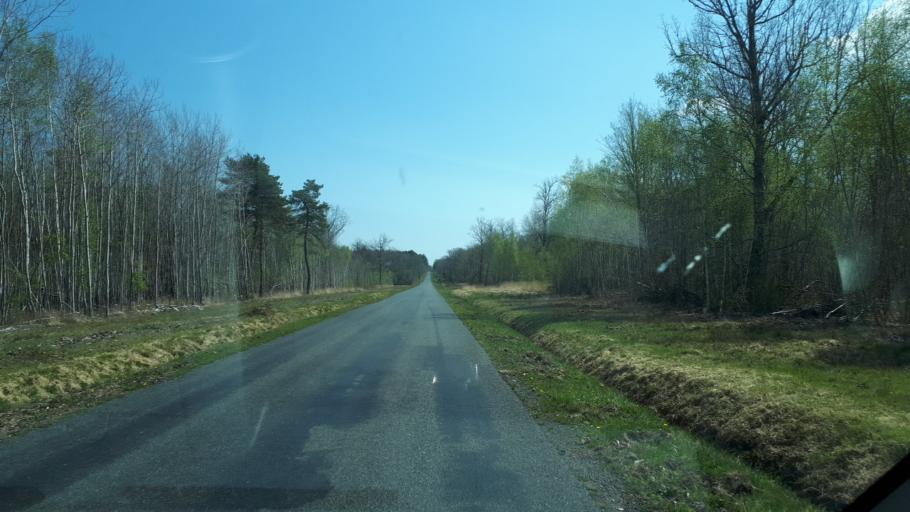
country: FR
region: Centre
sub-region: Departement du Cher
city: Neuvy-sur-Barangeon
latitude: 47.3189
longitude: 2.1638
